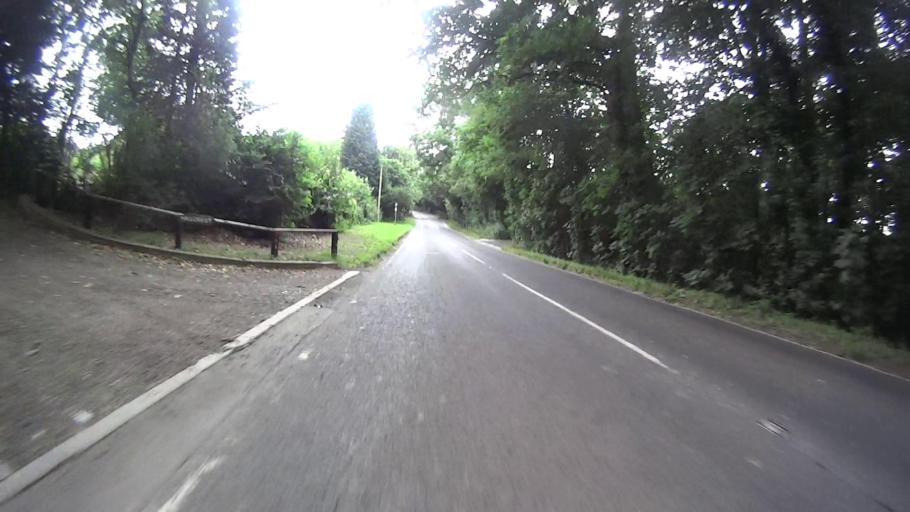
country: GB
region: England
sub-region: Surrey
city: Reigate
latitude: 51.1936
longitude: -0.2414
